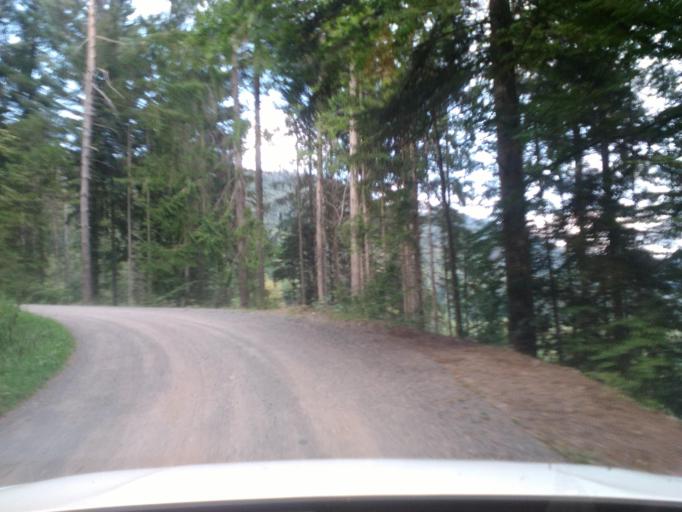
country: FR
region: Lorraine
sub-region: Departement des Vosges
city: Senones
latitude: 48.4079
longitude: 6.9756
